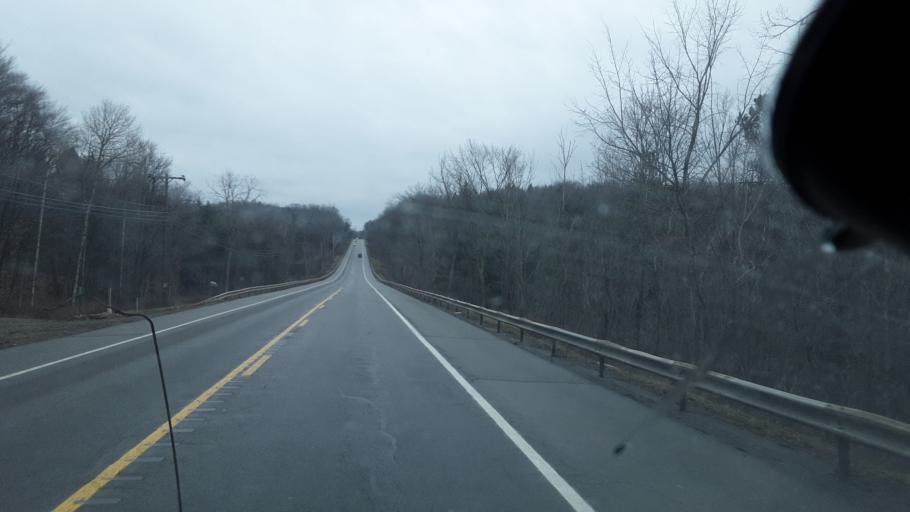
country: US
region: New York
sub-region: Erie County
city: Holland
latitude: 42.6118
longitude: -78.5067
